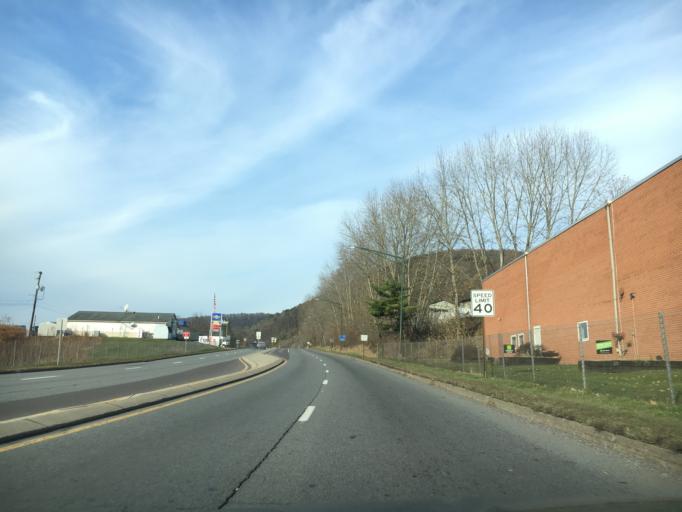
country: US
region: Pennsylvania
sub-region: Montour County
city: Danville
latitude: 40.9681
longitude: -76.6162
